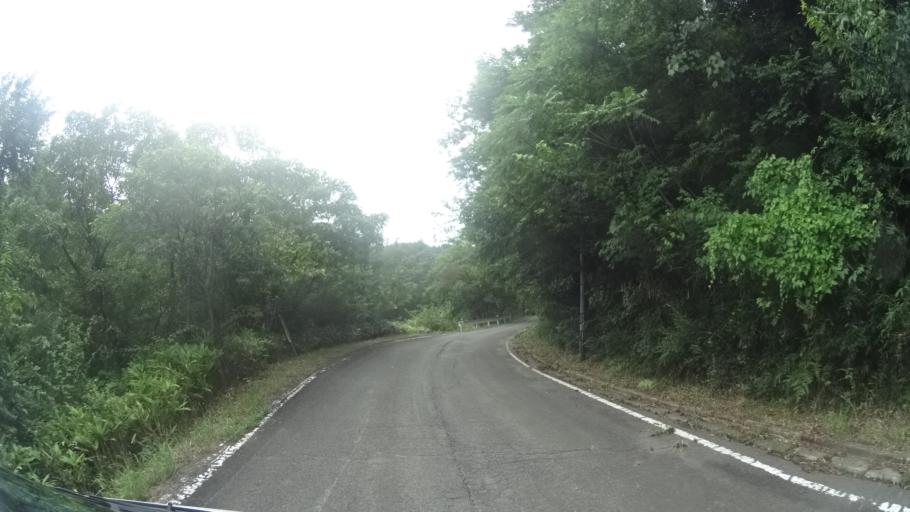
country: JP
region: Kyoto
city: Maizuru
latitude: 35.3531
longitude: 135.3435
